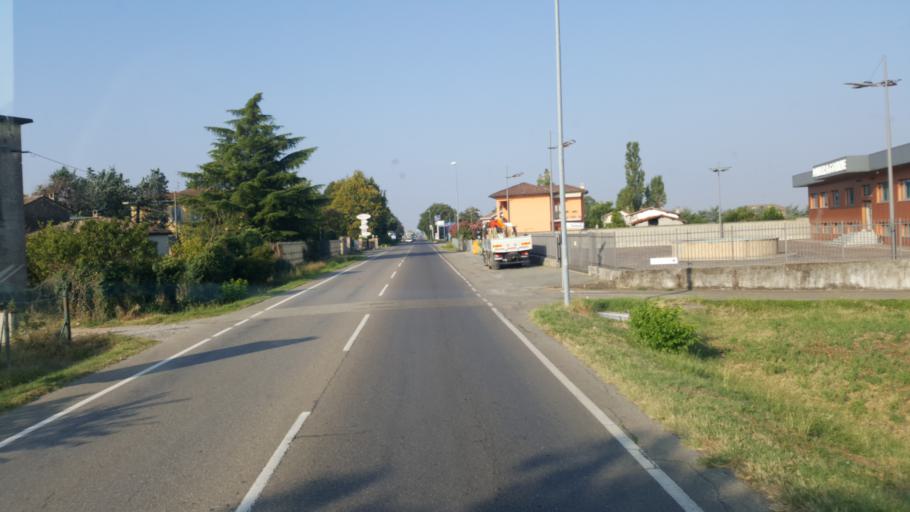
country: IT
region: Lombardy
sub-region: Provincia di Pavia
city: Voghera
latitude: 44.9835
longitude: 8.9833
